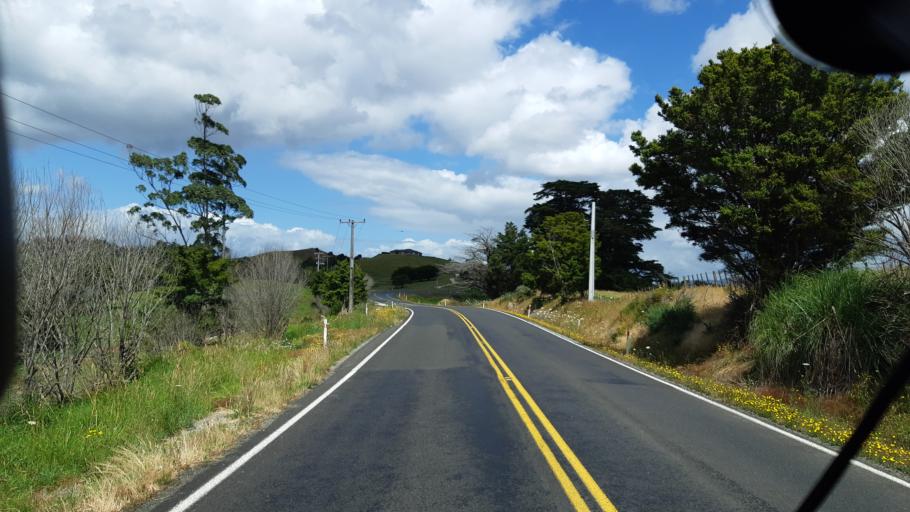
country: NZ
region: Northland
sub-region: Far North District
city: Waimate North
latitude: -35.3014
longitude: 173.5948
